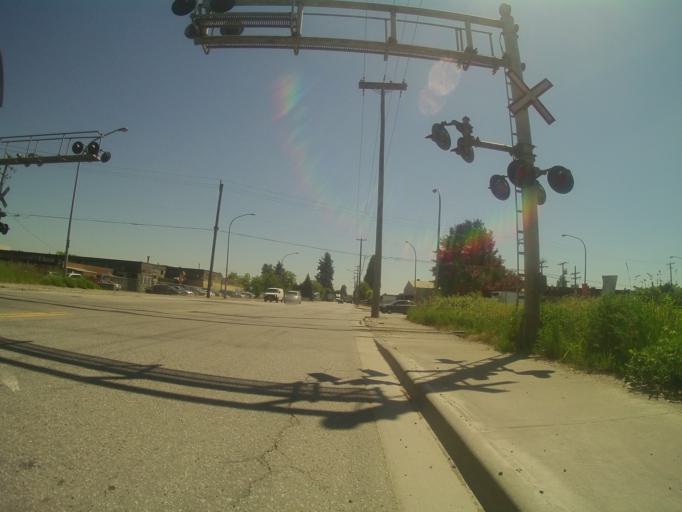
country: CA
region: British Columbia
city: Vancouver
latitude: 49.1991
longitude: -123.0693
